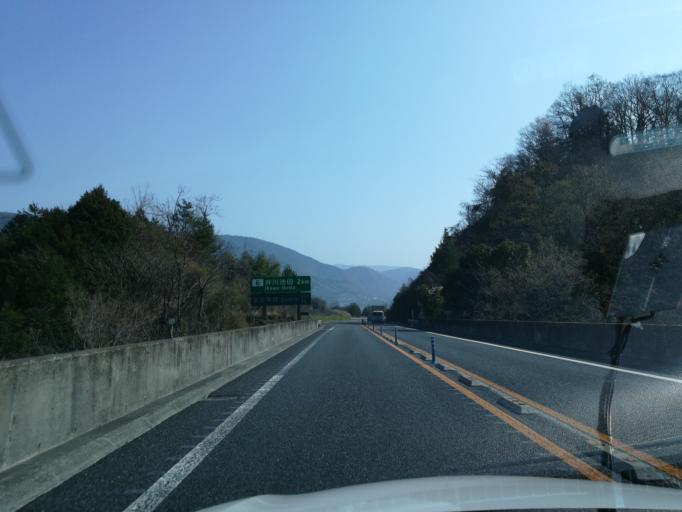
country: JP
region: Tokushima
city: Ikedacho
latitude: 34.0231
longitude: 133.8173
